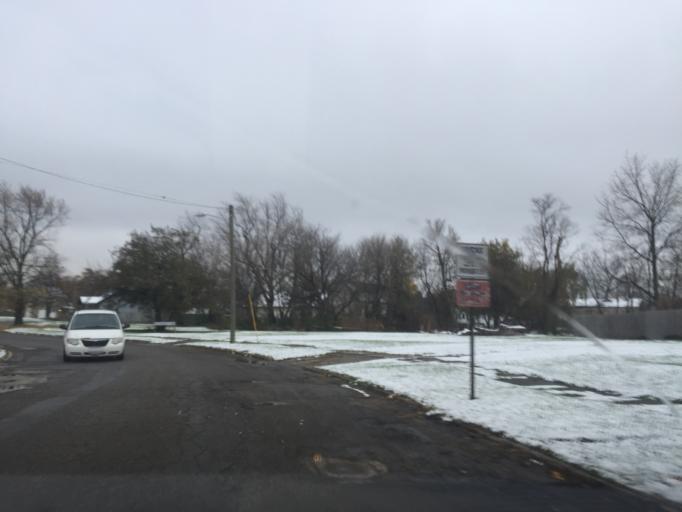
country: US
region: Michigan
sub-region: Oakland County
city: Pontiac
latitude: 42.6244
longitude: -83.2790
